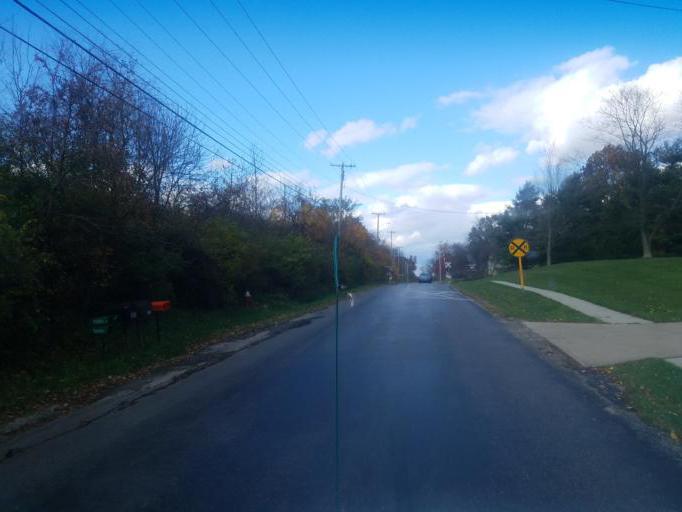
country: US
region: Ohio
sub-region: Wayne County
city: Orrville
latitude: 40.8317
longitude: -81.7745
